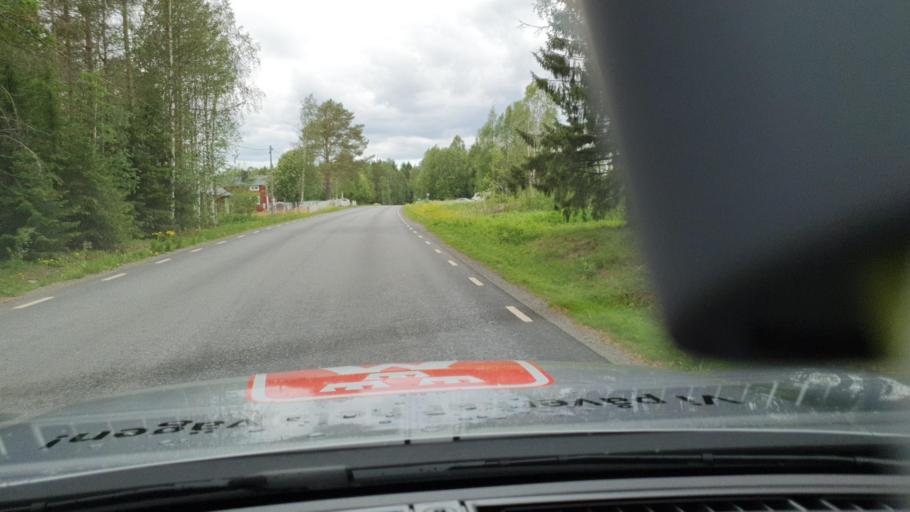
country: SE
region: Norrbotten
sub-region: Lulea Kommun
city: Gammelstad
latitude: 65.7882
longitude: 22.0879
